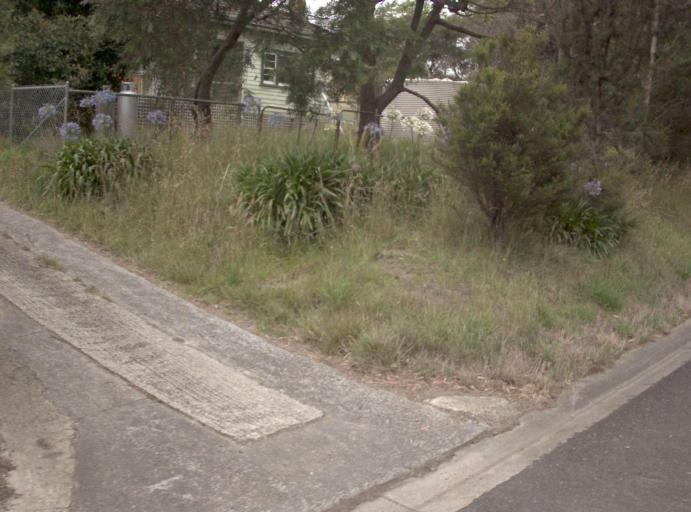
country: AU
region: Victoria
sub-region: Yarra Ranges
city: Yarra Glen
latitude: -37.5809
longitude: 145.4120
